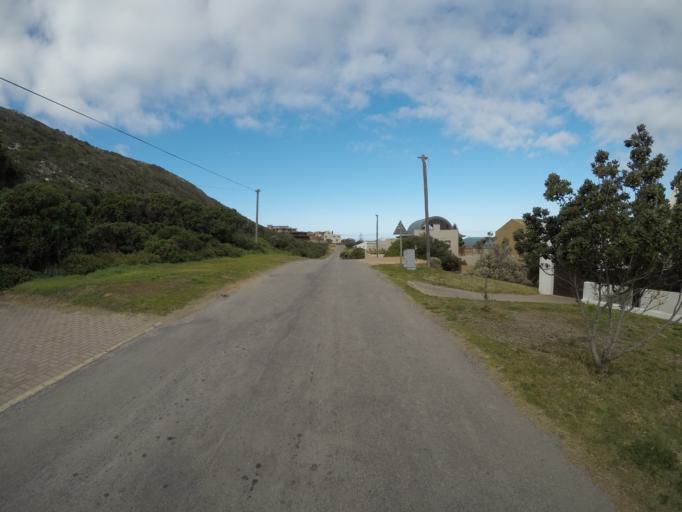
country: ZA
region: Western Cape
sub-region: Eden District Municipality
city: Riversdale
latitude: -34.4310
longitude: 21.3275
